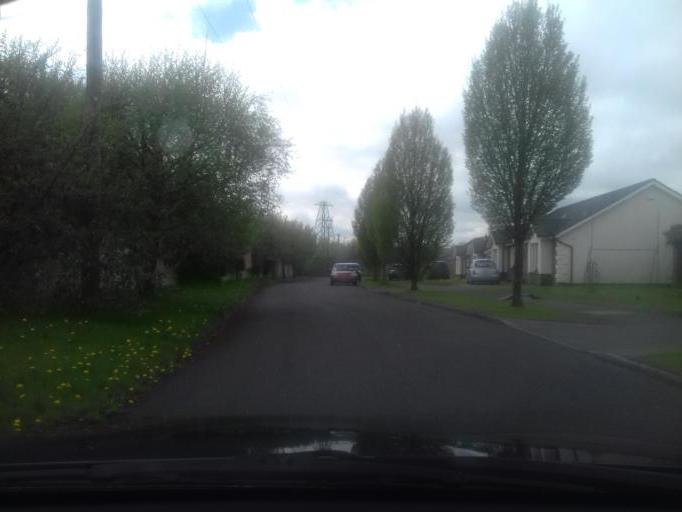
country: IE
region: Leinster
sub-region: Laois
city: Portlaoise
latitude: 53.0421
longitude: -7.3137
